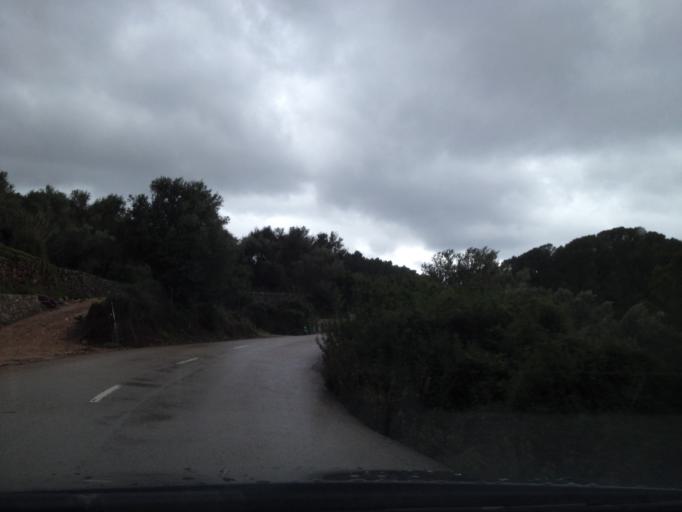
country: ES
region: Balearic Islands
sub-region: Illes Balears
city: Soller
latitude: 39.7734
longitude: 2.6822
